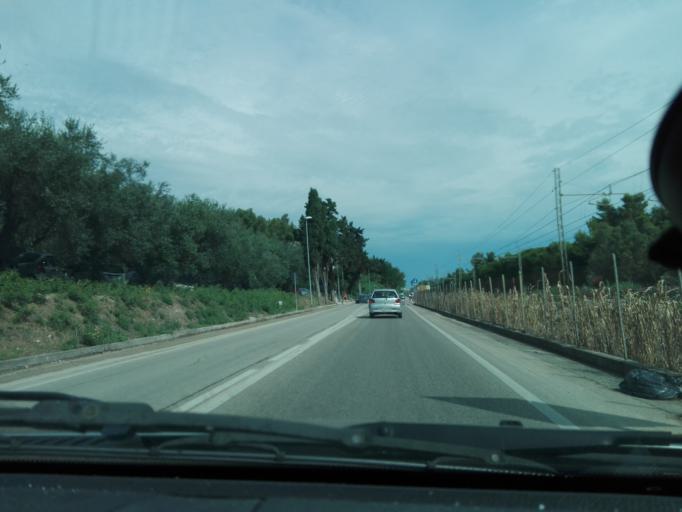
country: IT
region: Abruzzo
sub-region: Provincia di Teramo
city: Pineto
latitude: 42.5890
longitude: 14.0846
